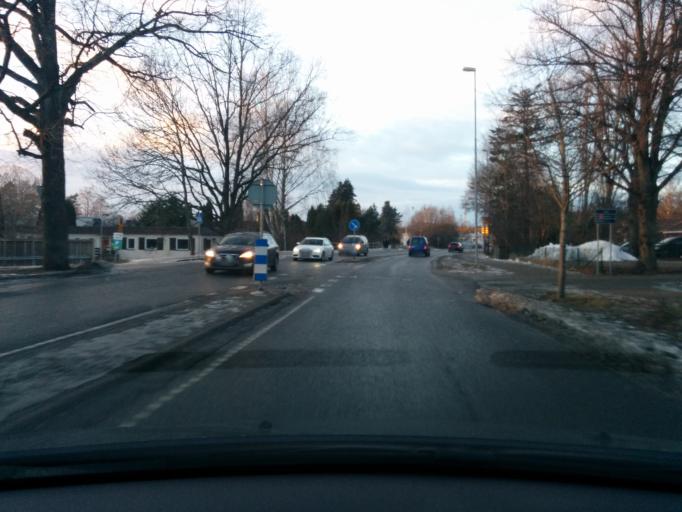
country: SE
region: Stockholm
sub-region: Nacka Kommun
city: Alta
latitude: 59.2616
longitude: 18.1837
